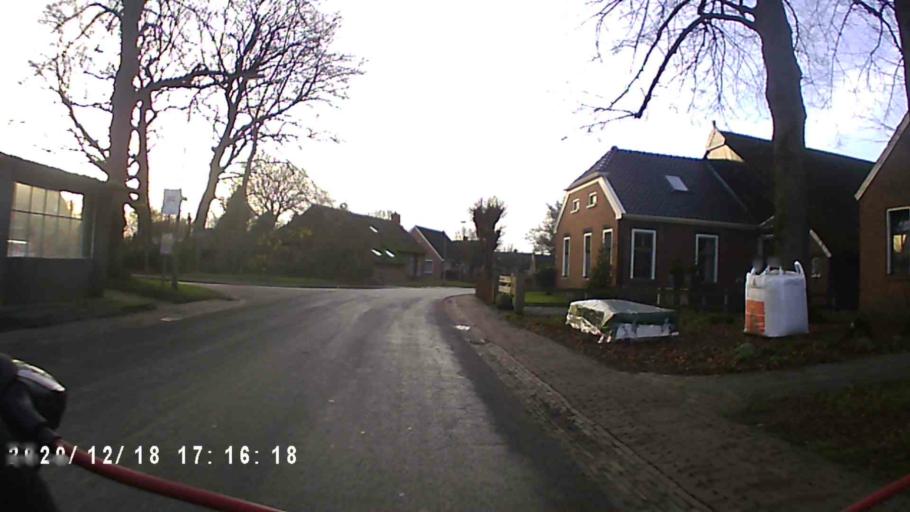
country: NL
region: Drenthe
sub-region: Gemeente Tynaarlo
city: Tynaarlo
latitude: 53.0783
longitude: 6.6165
